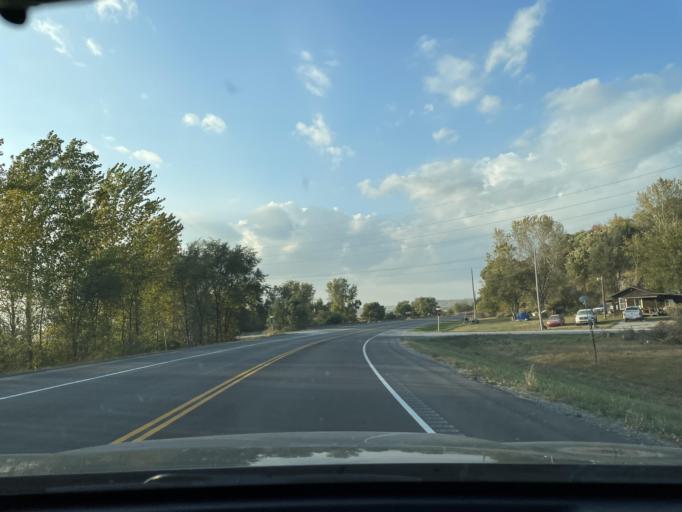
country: US
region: Missouri
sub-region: Andrew County
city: Country Club Village
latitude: 39.8596
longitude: -94.8796
